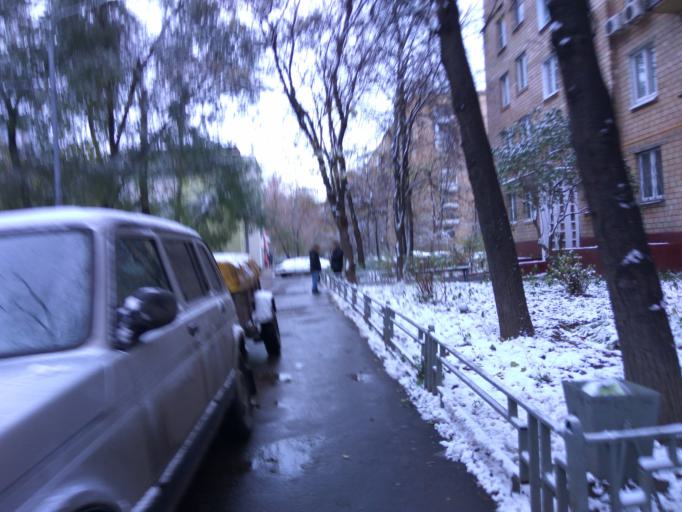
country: RU
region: Moscow
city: Kolomenskoye
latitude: 55.6740
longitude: 37.6660
